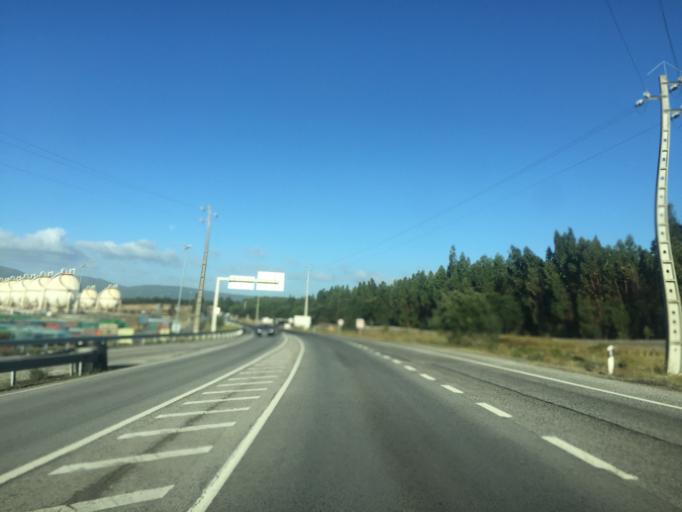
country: PT
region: Lisbon
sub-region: Azambuja
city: Aveiras de Cima
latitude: 39.1710
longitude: -8.9254
